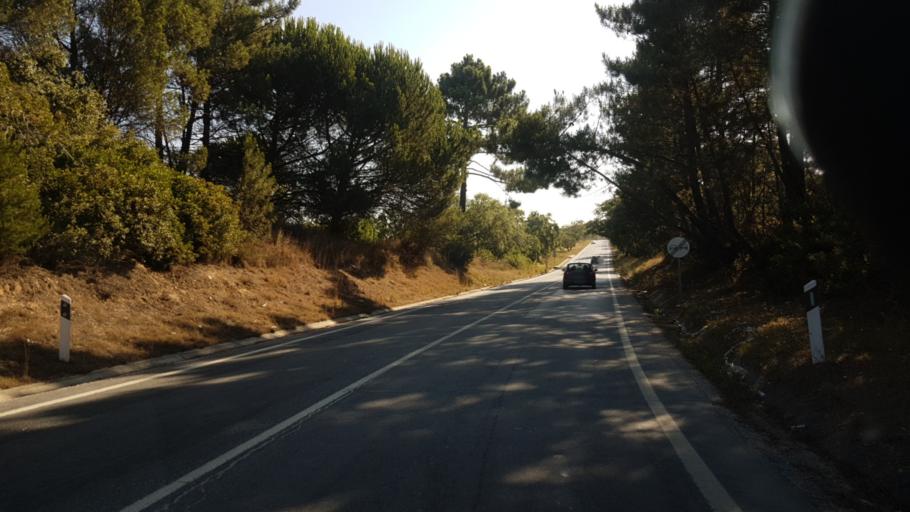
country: PT
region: Setubal
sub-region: Sesimbra
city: Sesimbra
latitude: 38.4811
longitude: -9.0732
